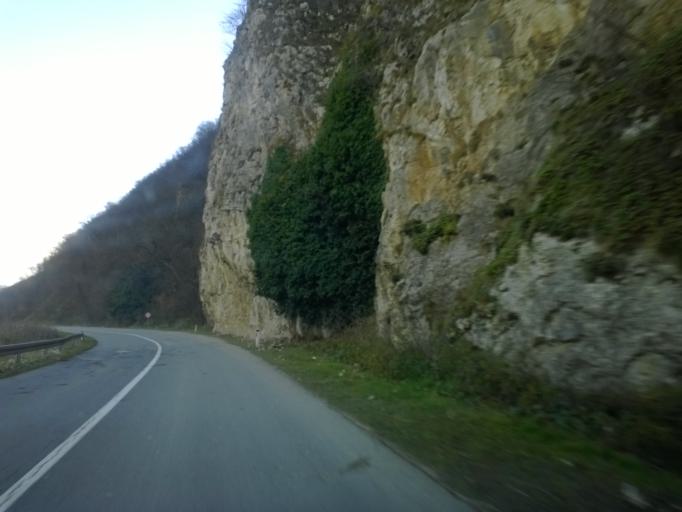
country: RO
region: Caras-Severin
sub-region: Comuna Pescari
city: Coronini
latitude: 44.6529
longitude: 21.7384
